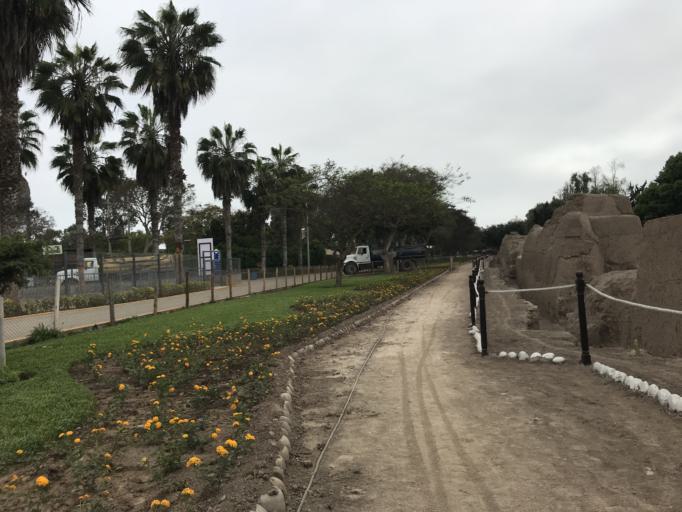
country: PE
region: Callao
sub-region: Callao
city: Callao
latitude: -12.0675
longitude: -77.0867
